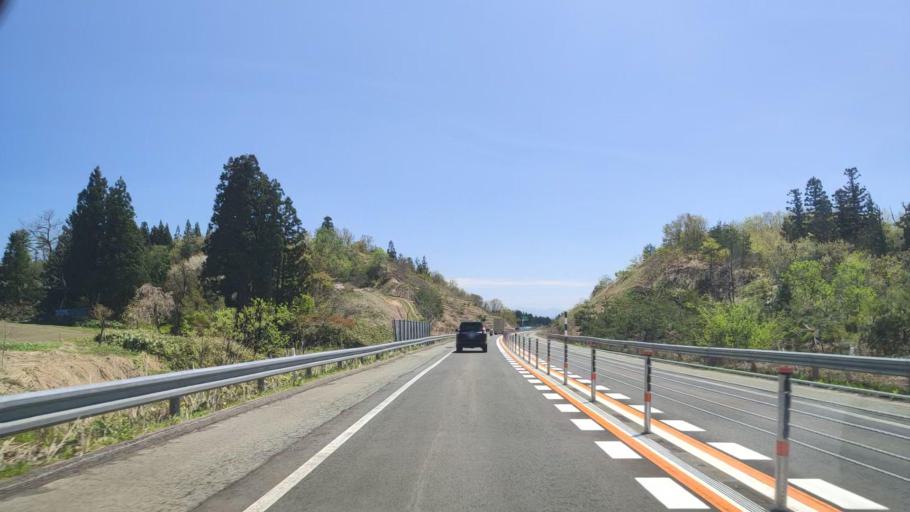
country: JP
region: Yamagata
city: Obanazawa
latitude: 38.6449
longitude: 140.3731
